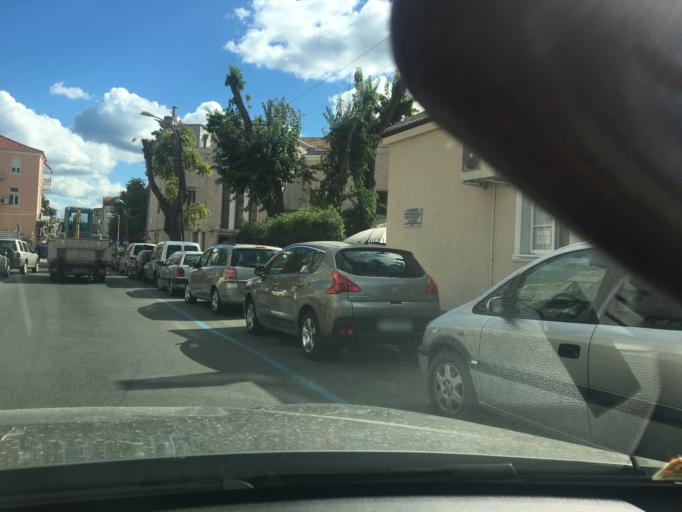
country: BG
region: Burgas
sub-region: Obshtina Burgas
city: Burgas
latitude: 42.4972
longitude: 27.4733
